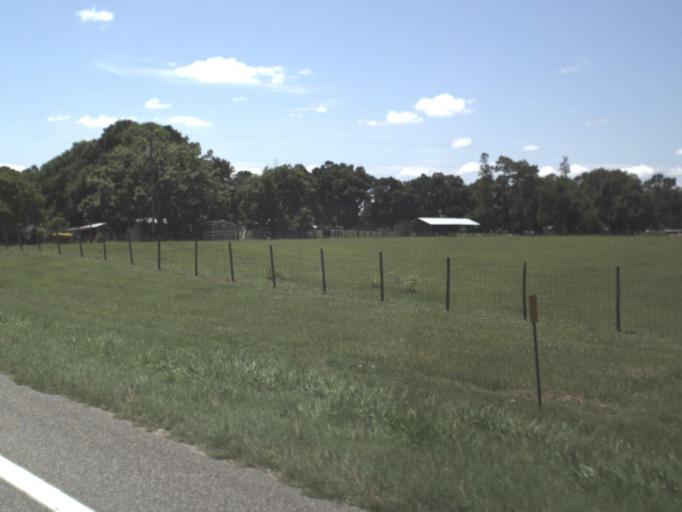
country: US
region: Florida
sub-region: Lafayette County
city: Mayo
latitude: 30.0533
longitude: -83.1102
